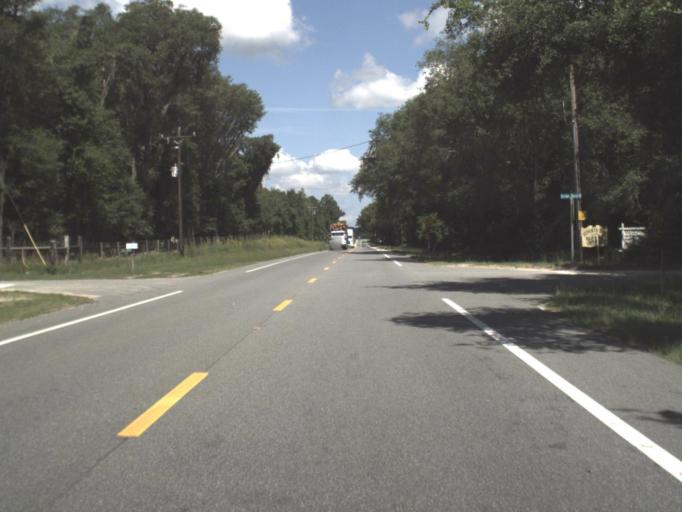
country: US
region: Florida
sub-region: Putnam County
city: Interlachen
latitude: 29.7085
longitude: -81.7868
